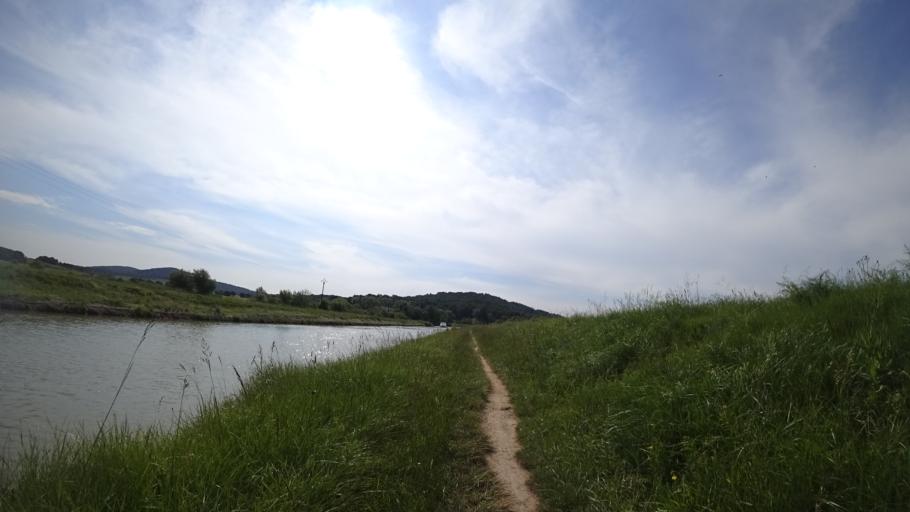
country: FR
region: Languedoc-Roussillon
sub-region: Departement de l'Herault
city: Olonzac
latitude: 43.2635
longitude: 2.7461
